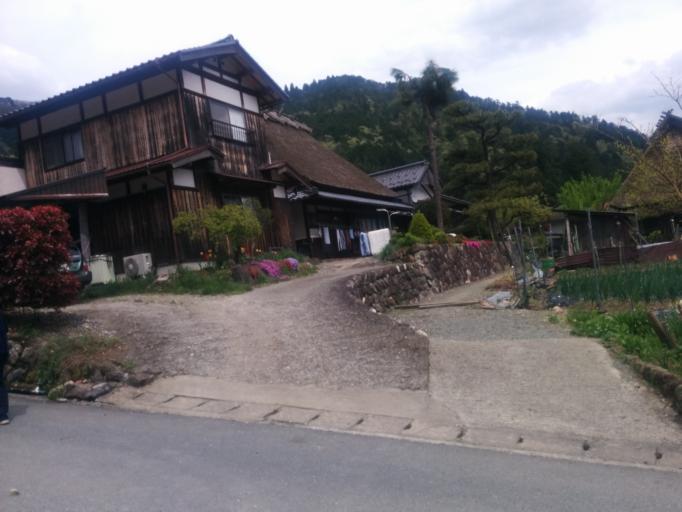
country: JP
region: Fukui
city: Obama
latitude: 35.3134
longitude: 135.6225
